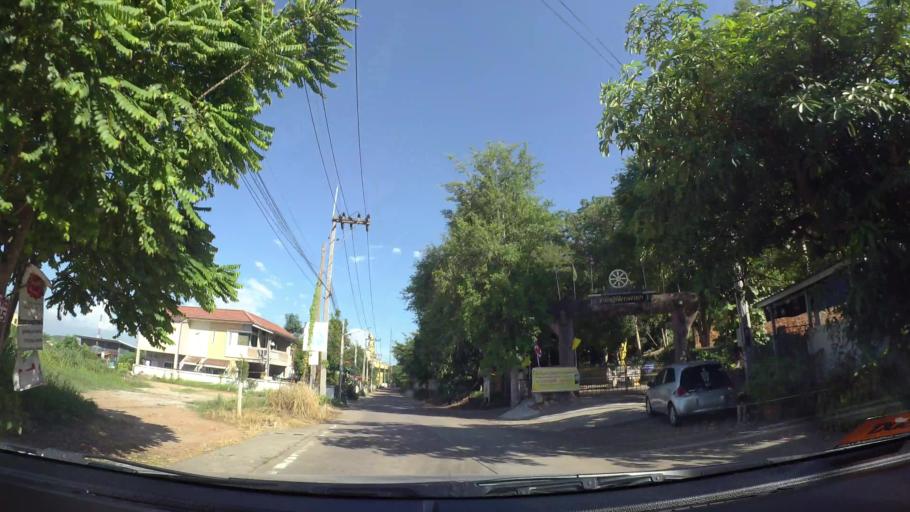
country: TH
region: Chon Buri
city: Si Racha
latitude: 13.1553
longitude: 100.9299
